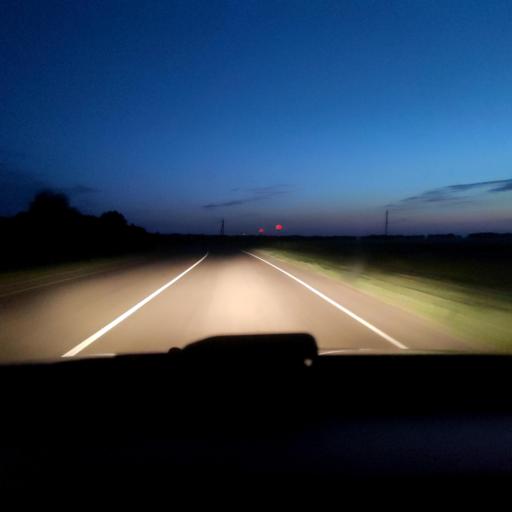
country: RU
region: Voronezj
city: Panino
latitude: 51.5739
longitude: 39.9100
